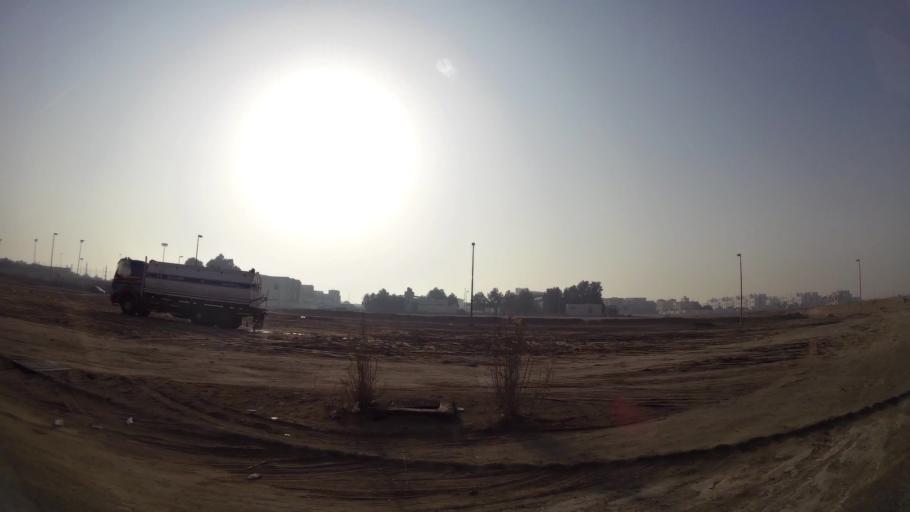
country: AE
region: Abu Dhabi
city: Abu Dhabi
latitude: 24.2832
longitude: 54.6405
